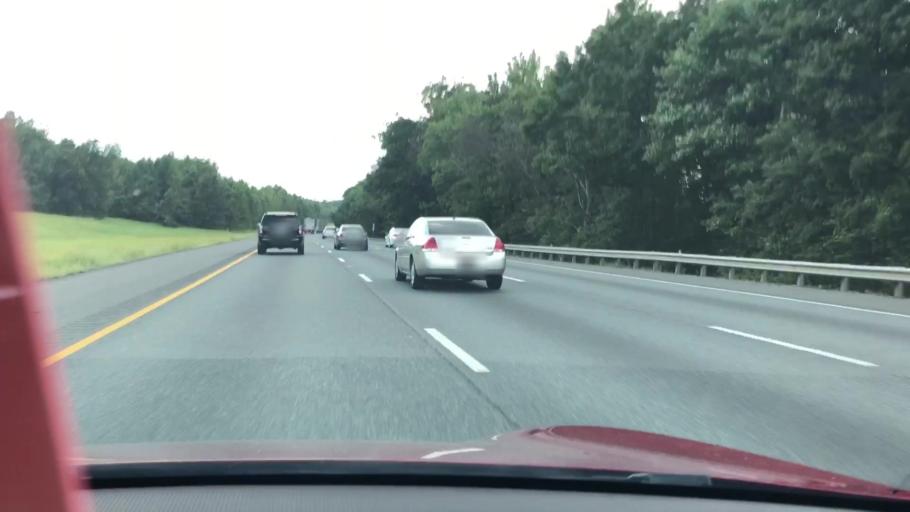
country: US
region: Maryland
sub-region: Harford County
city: Riverside
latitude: 39.4749
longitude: -76.2738
